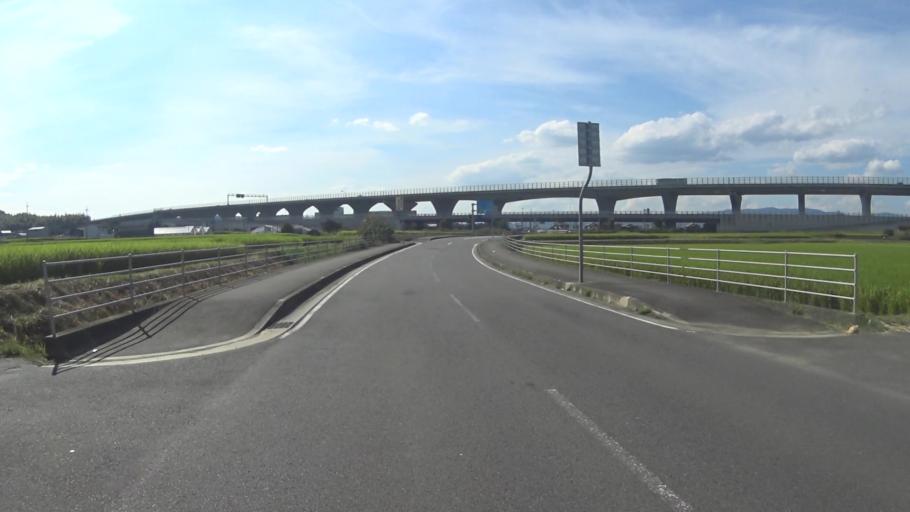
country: JP
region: Kyoto
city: Yawata
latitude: 34.8497
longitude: 135.7333
